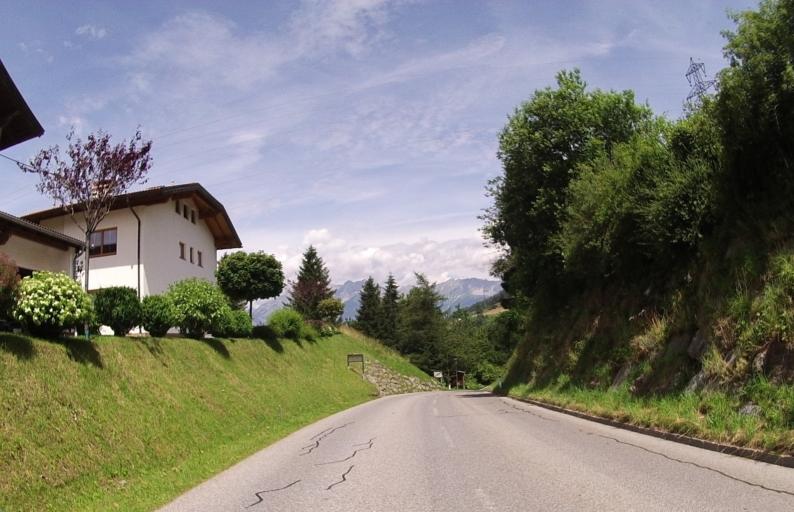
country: AT
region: Tyrol
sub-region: Politischer Bezirk Innsbruck Land
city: Schoenberg im Stubaital
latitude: 47.1869
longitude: 11.4291
